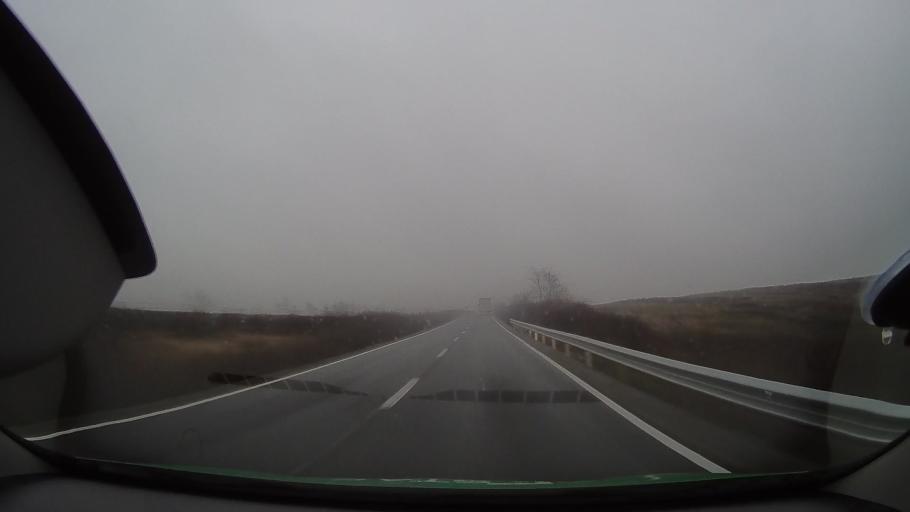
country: RO
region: Bihor
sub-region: Comuna Olcea
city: Olcea
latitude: 46.6782
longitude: 21.9657
